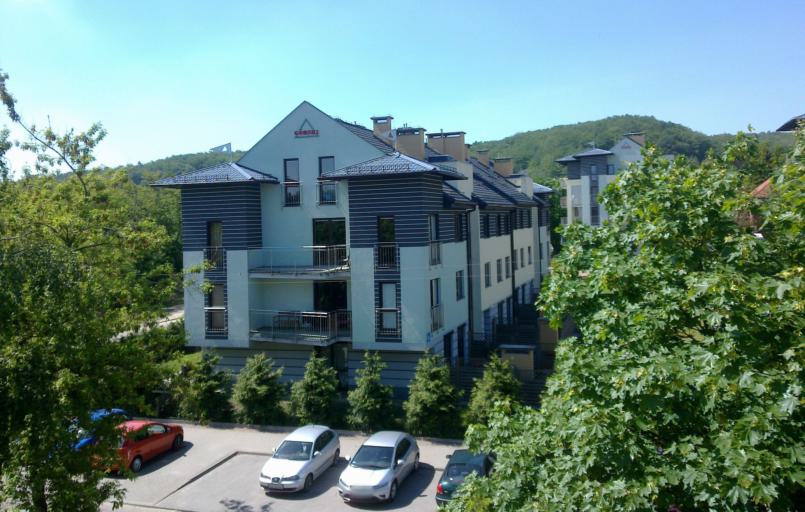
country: PL
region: Pomeranian Voivodeship
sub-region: Sopot
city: Sopot
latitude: 54.4040
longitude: 18.5674
